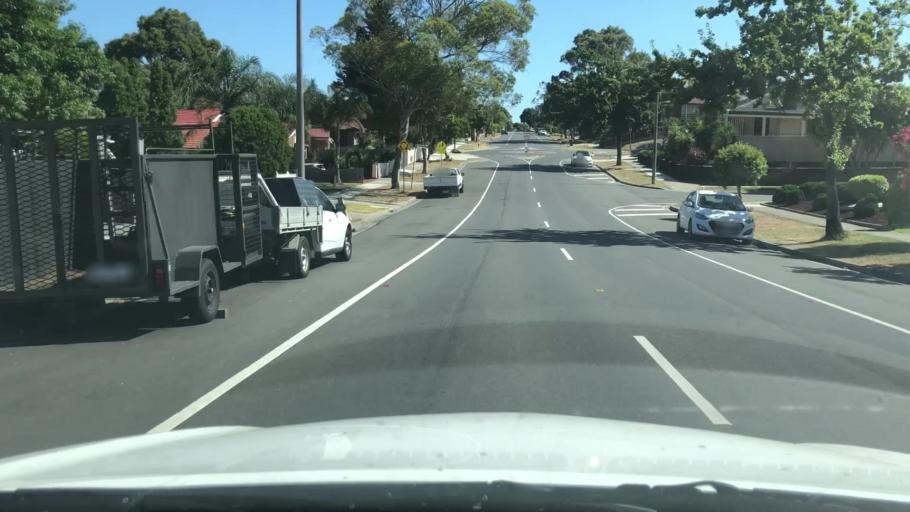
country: AU
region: Victoria
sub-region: Casey
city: Endeavour Hills
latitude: -37.9784
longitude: 145.2700
